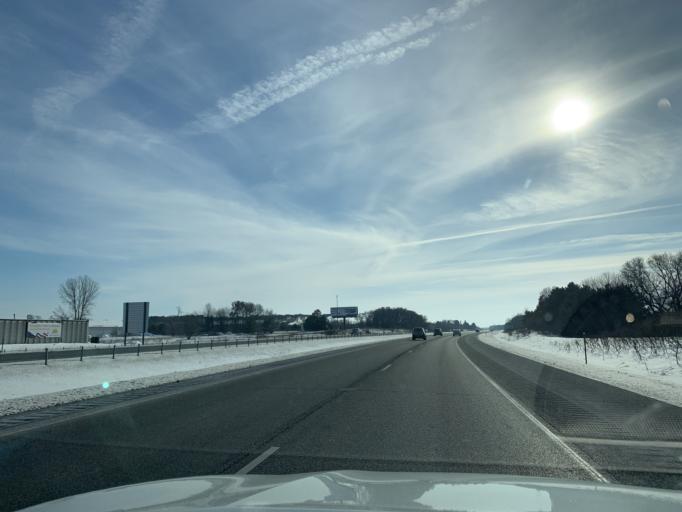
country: US
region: Minnesota
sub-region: Chisago County
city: Wyoming
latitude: 45.3255
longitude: -93.0037
